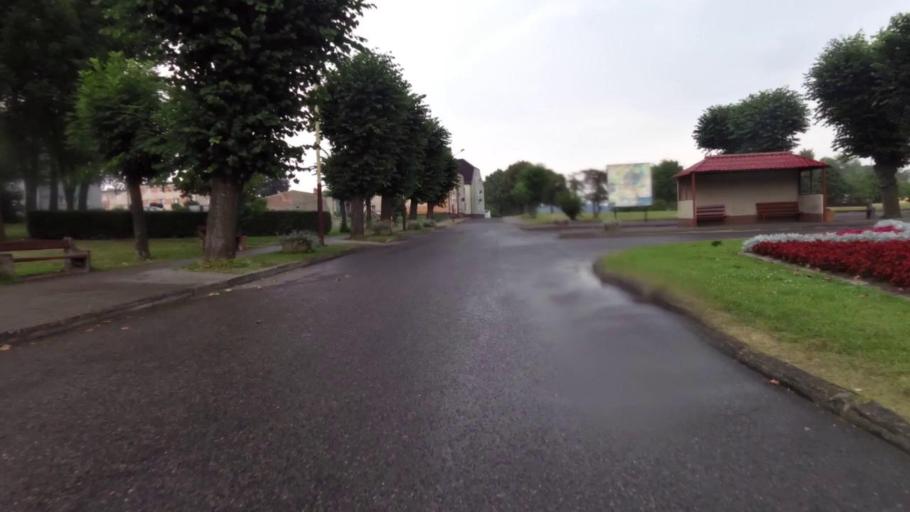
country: PL
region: West Pomeranian Voivodeship
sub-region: Powiat stargardzki
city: Insko
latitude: 53.4365
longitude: 15.5469
